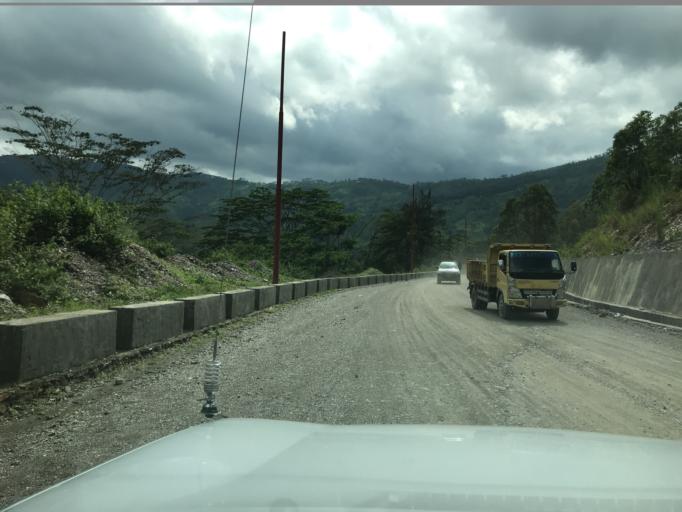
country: TL
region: Aileu
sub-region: Aileu Villa
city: Aileu
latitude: -8.6587
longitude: 125.5316
